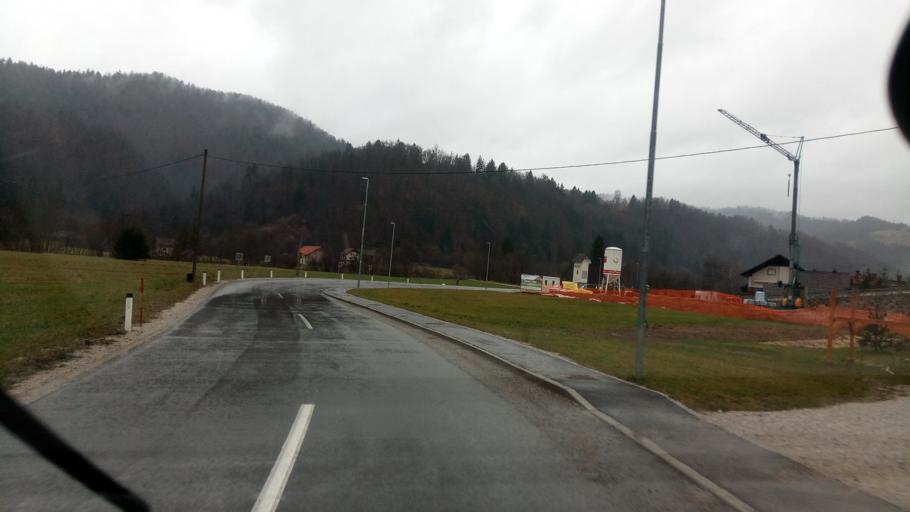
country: SI
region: Vrhnika
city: Vrhnika
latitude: 45.9970
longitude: 14.2416
